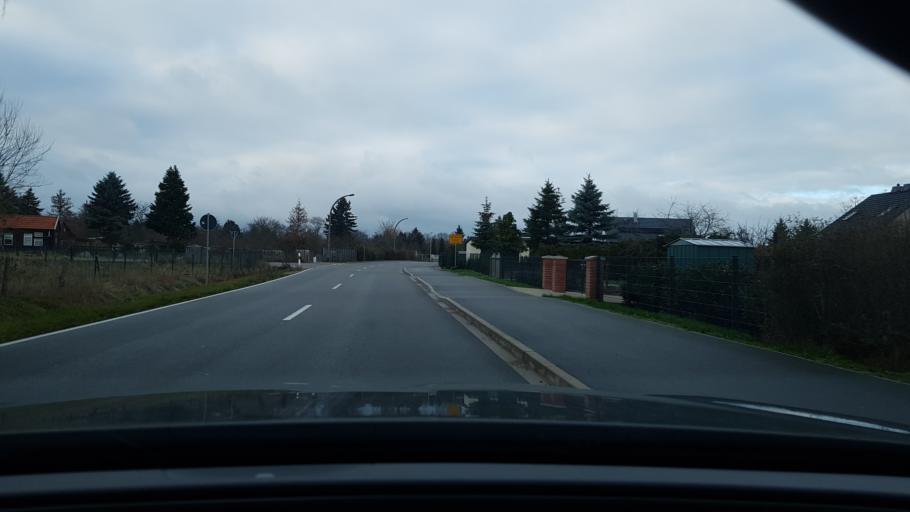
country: DE
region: Saxony-Anhalt
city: Oebisfelde
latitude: 52.4265
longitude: 10.9961
